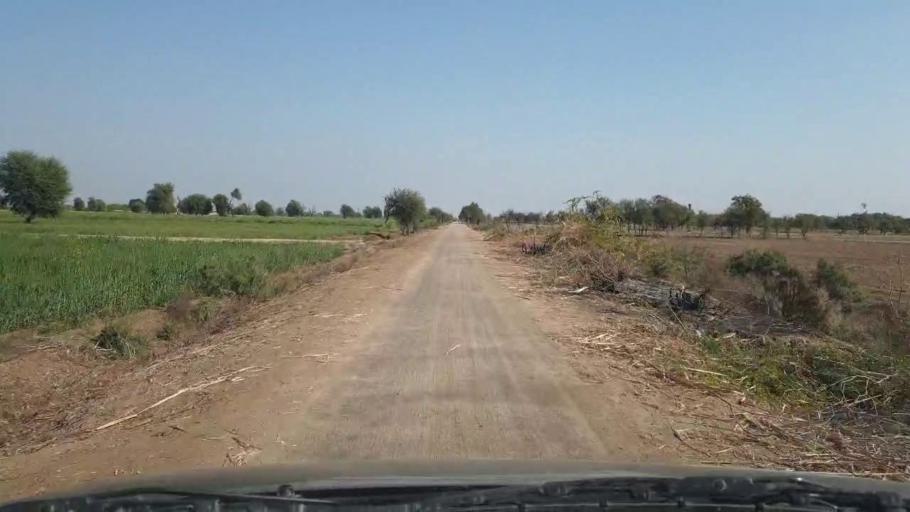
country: PK
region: Sindh
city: Samaro
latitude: 25.1929
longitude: 69.2828
